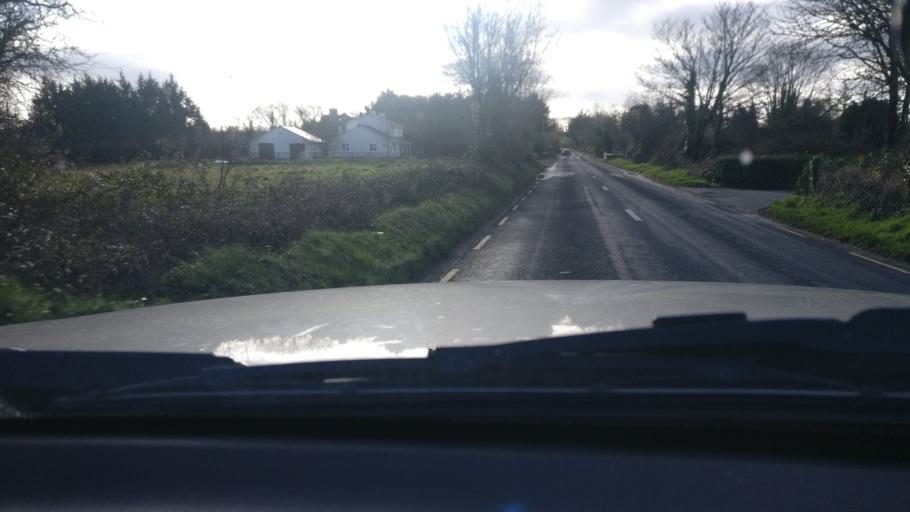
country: IE
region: Connaught
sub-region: County Galway
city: Ballinasloe
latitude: 53.3115
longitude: -8.2408
